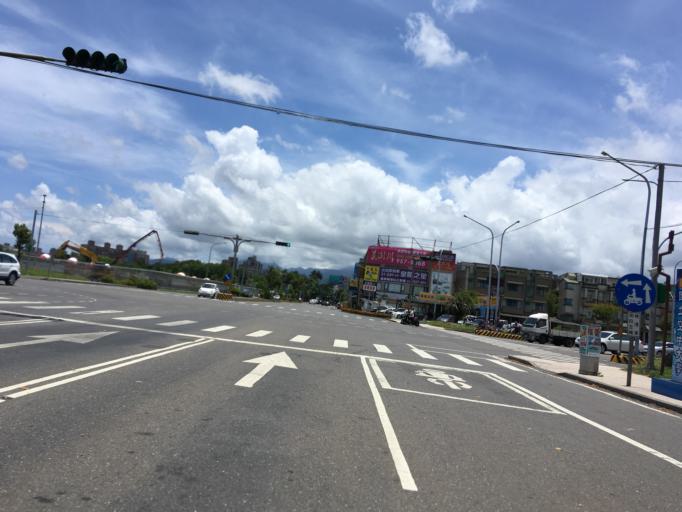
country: TW
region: Taiwan
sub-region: Yilan
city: Yilan
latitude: 24.6879
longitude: 121.7705
